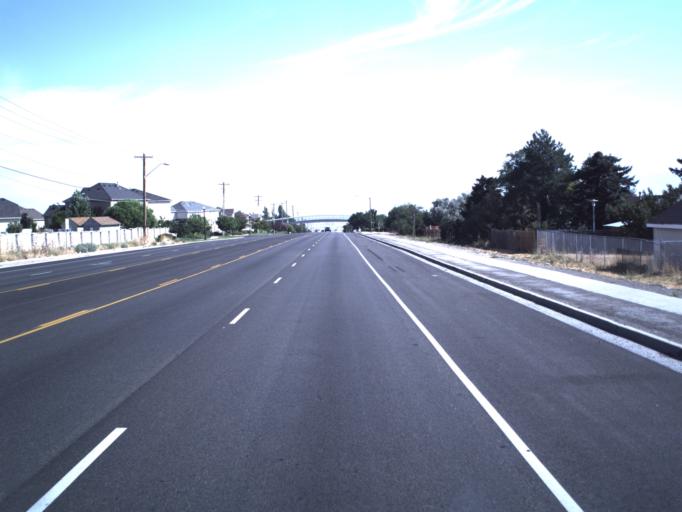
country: US
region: Utah
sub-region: Salt Lake County
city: Oquirrh
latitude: 40.6548
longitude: -112.0246
